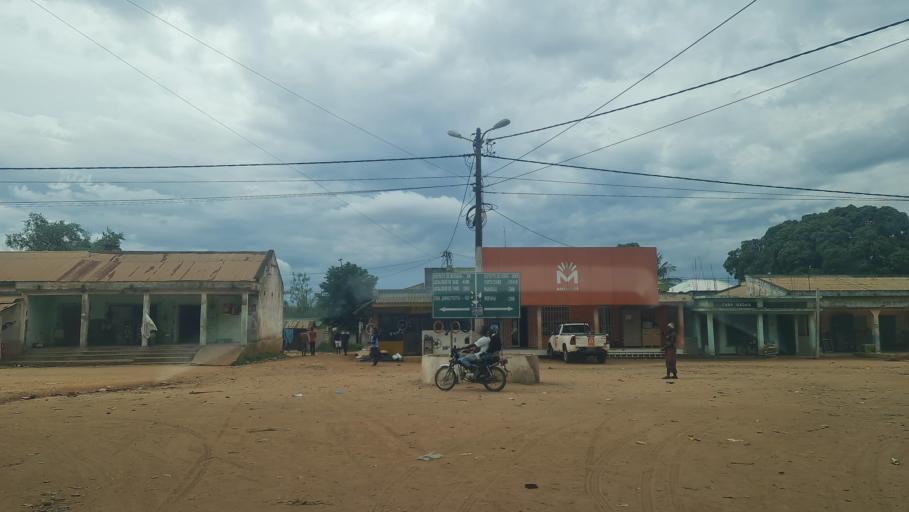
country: MW
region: Southern Region
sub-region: Nsanje District
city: Nsanje
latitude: -17.3278
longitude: 35.5901
